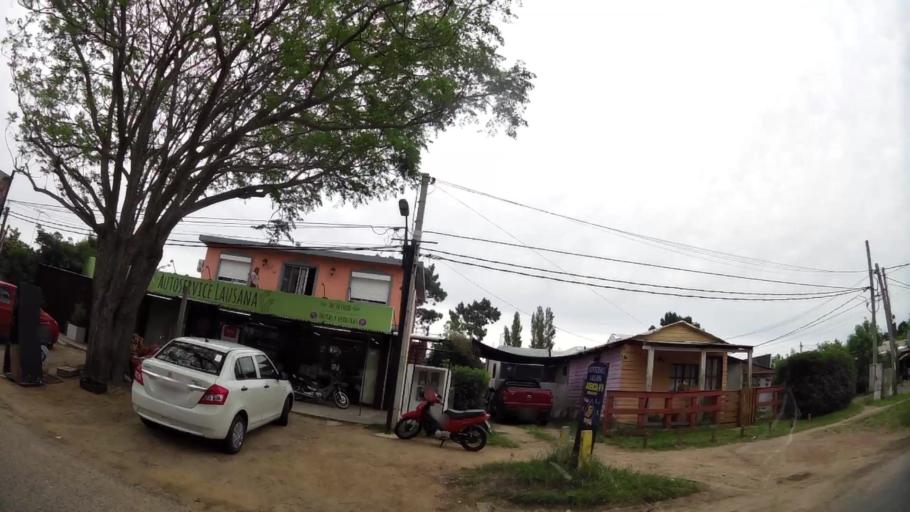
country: UY
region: Maldonado
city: Maldonado
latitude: -34.9000
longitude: -54.9935
